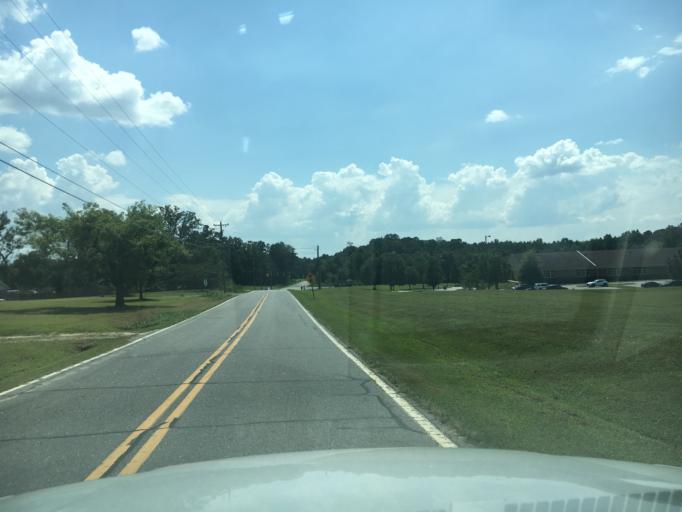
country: US
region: North Carolina
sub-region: Rutherford County
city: Forest City
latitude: 35.2714
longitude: -81.8441
